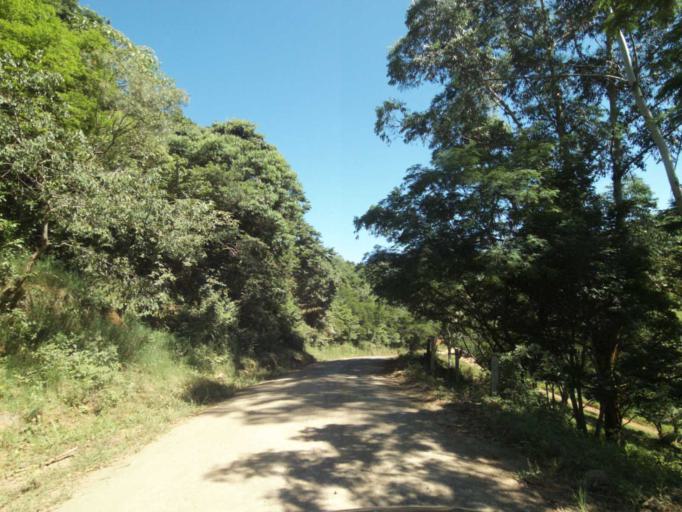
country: BR
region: Parana
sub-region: Francisco Beltrao
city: Francisco Beltrao
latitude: -26.1493
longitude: -53.3039
